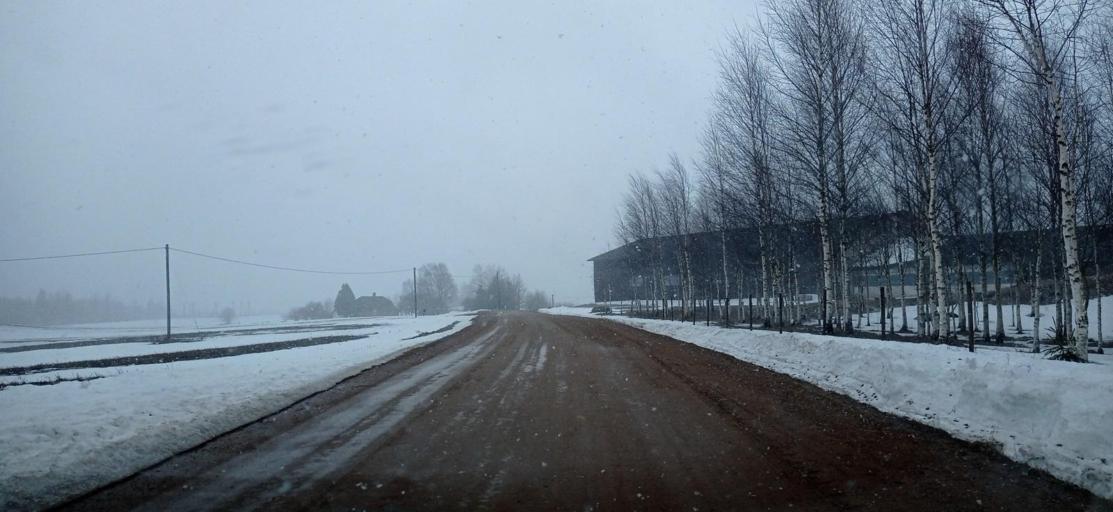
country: EE
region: Tartu
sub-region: Noo vald
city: Noo
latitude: 58.0911
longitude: 26.6636
